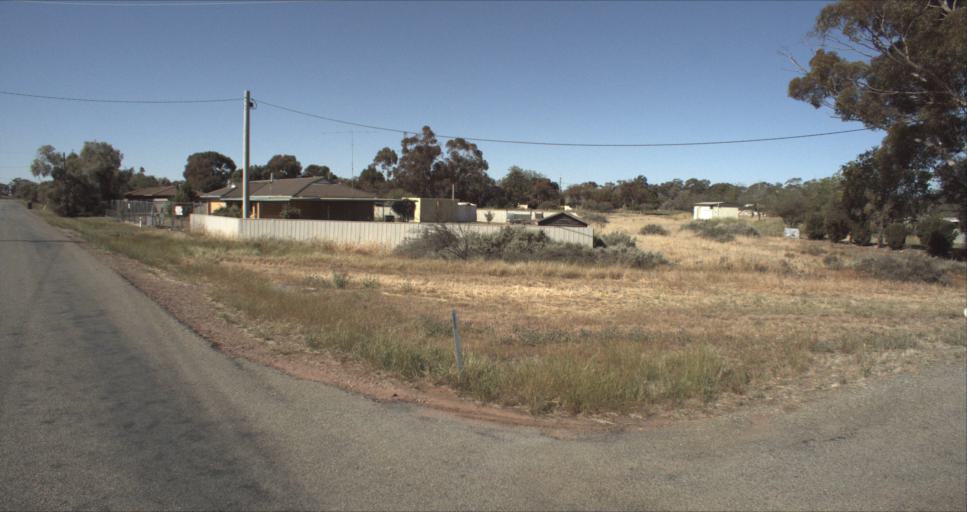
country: AU
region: New South Wales
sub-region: Leeton
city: Leeton
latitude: -34.5562
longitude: 146.3844
